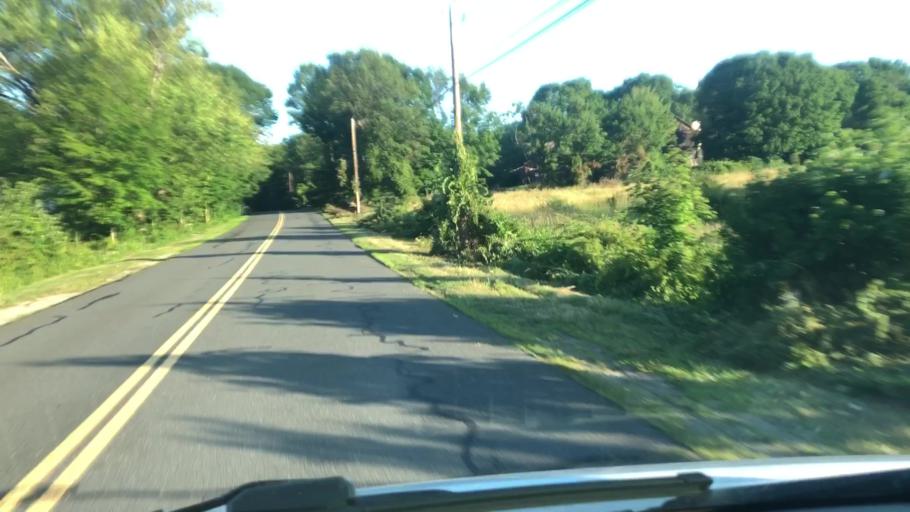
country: US
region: Massachusetts
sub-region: Hampshire County
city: Williamsburg
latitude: 42.3684
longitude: -72.7269
